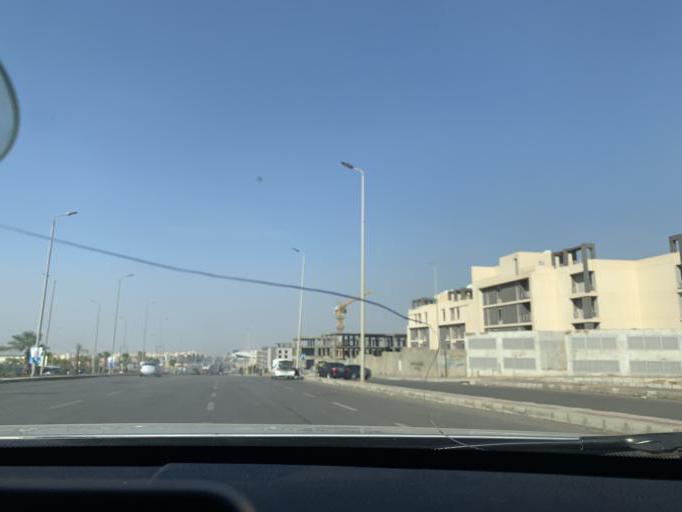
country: EG
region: Muhafazat al Qalyubiyah
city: Al Khankah
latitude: 30.0186
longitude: 31.4750
